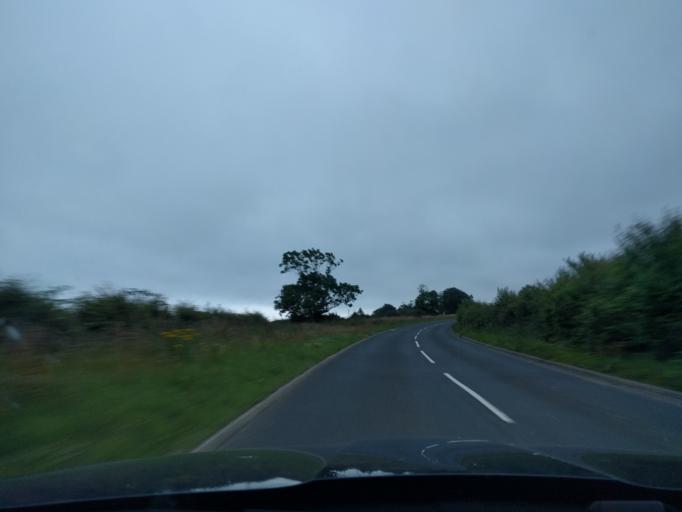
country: GB
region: England
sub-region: Northumberland
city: Acklington
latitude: 55.2471
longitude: -1.6471
